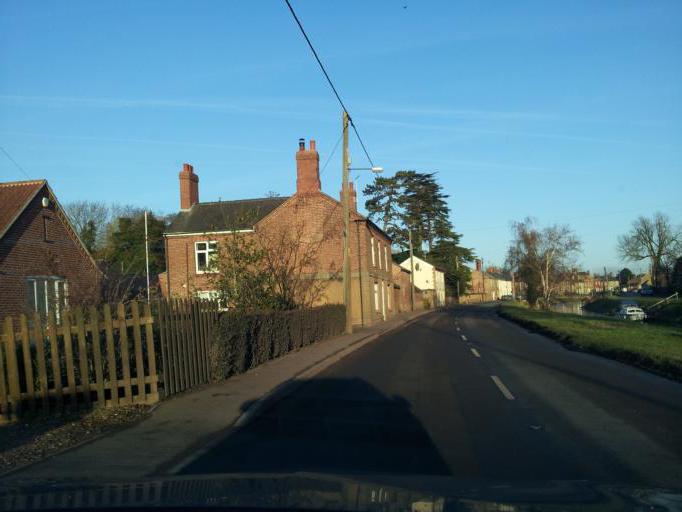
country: GB
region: England
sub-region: Norfolk
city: Outwell
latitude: 52.6004
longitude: 0.2138
